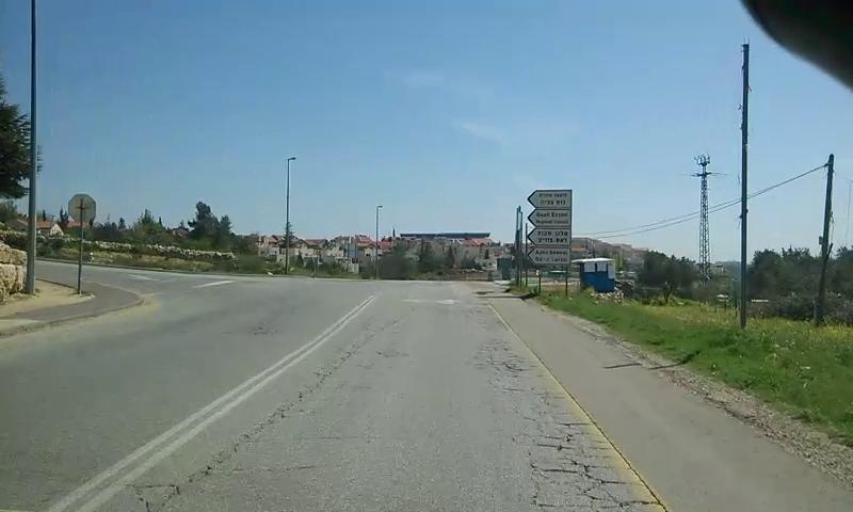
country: PS
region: West Bank
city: Nahhalin
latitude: 31.6545
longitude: 35.1226
